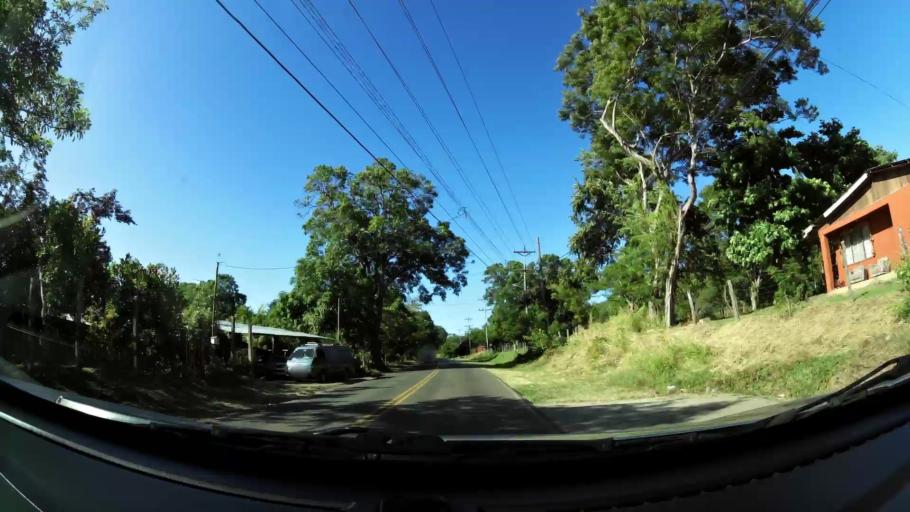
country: CR
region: Guanacaste
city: Belen
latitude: 10.3962
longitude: -85.6112
